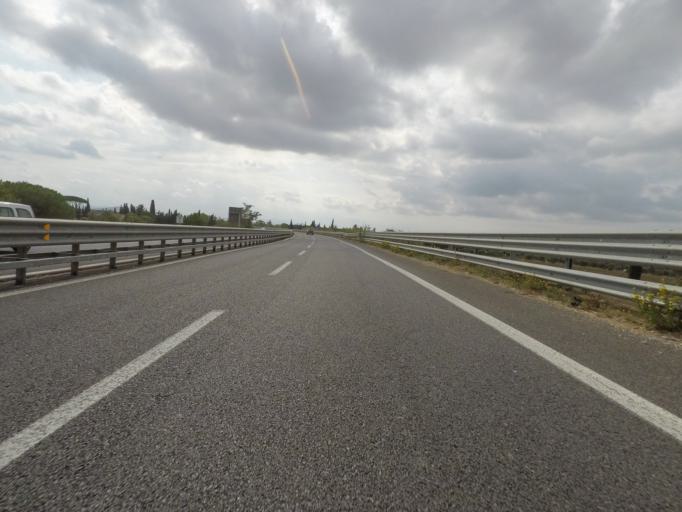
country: IT
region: Tuscany
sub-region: Provincia di Grosseto
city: Bagno Roselle
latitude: 42.8187
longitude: 11.1314
